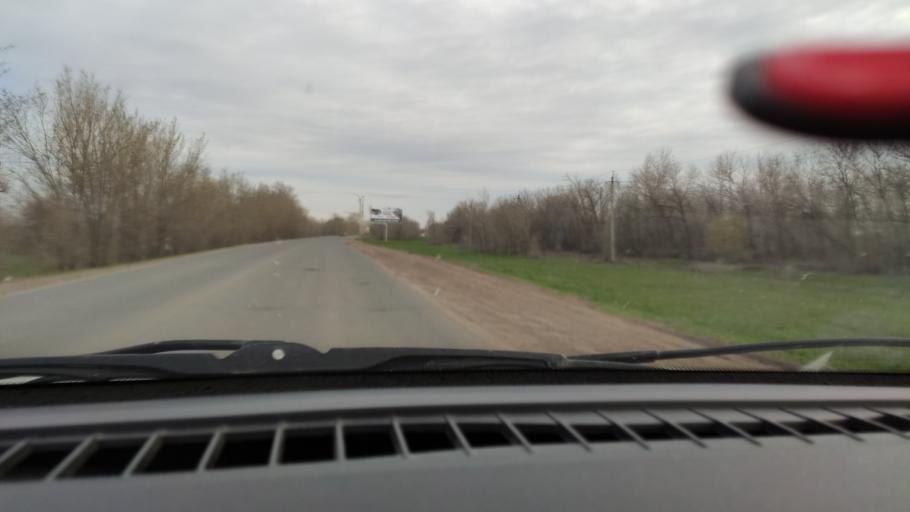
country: RU
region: Orenburg
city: Tatarskaya Kargala
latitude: 51.8869
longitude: 55.1558
